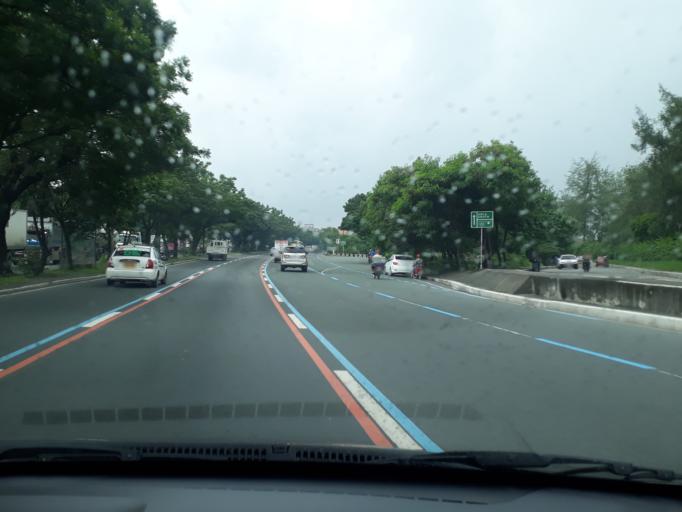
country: PH
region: Calabarzon
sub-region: Province of Rizal
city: Taguig
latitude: 14.5198
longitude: 121.0527
